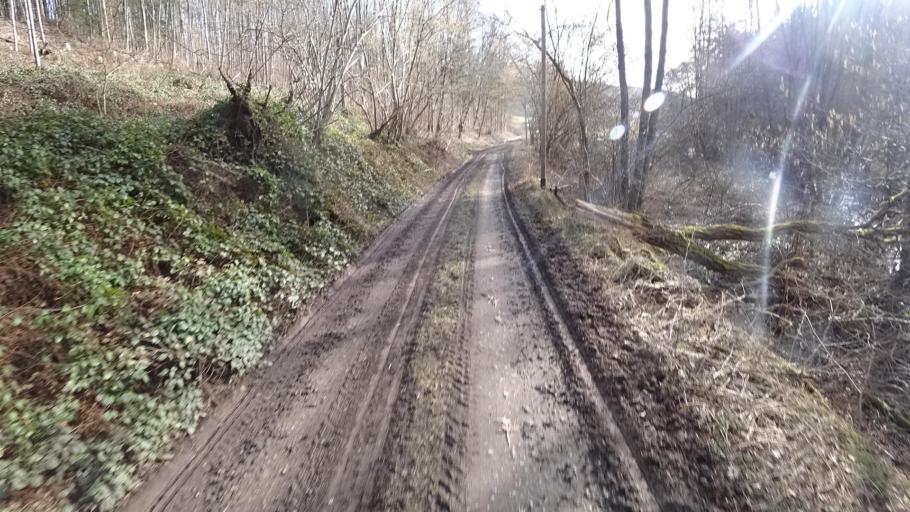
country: DE
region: Rheinland-Pfalz
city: Elben
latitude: 50.7666
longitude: 7.8370
